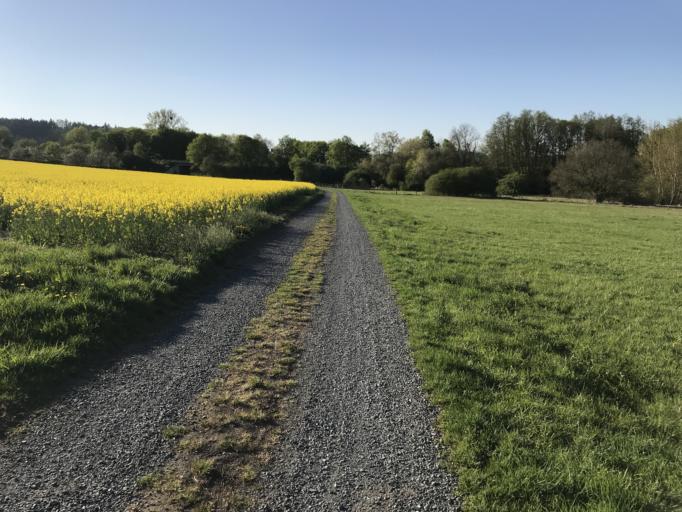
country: DE
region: Hesse
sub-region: Regierungsbezirk Giessen
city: Grossen Buseck
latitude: 50.5924
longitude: 8.8063
